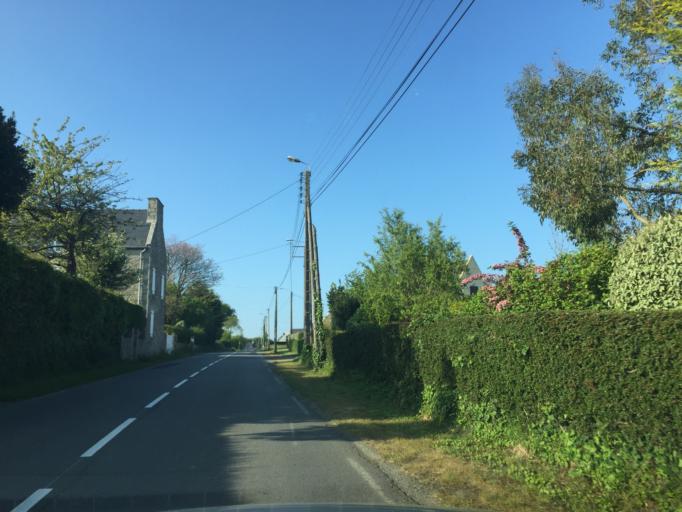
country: FR
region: Brittany
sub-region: Departement des Cotes-d'Armor
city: Saint-Cast-le-Guildo
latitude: 48.6102
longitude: -2.2549
